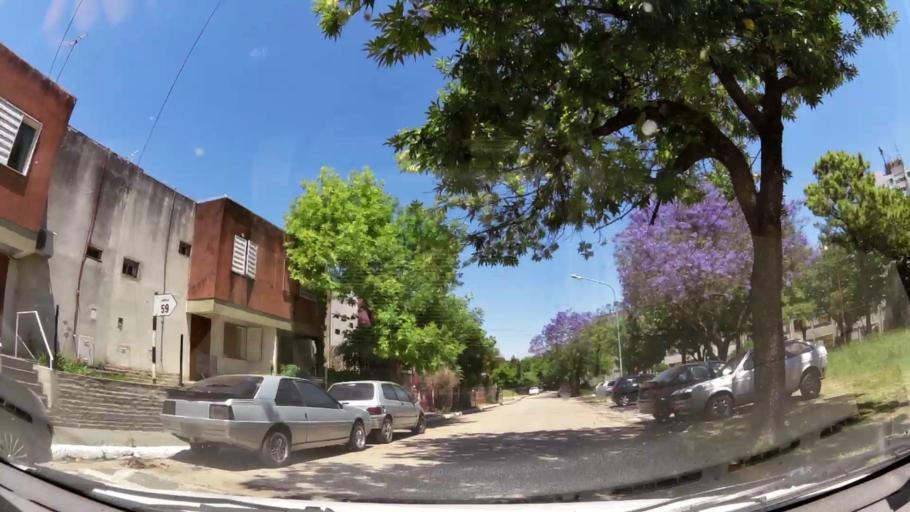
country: AR
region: Buenos Aires
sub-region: Partido de Merlo
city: Merlo
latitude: -34.6536
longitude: -58.7082
